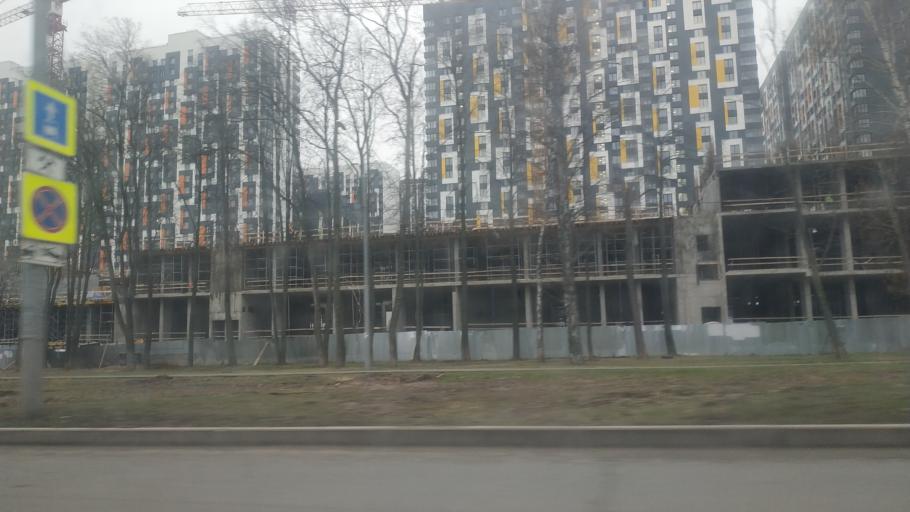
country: RU
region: Moskovskaya
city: Vostochnoe Degunino
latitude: 55.8810
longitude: 37.5443
